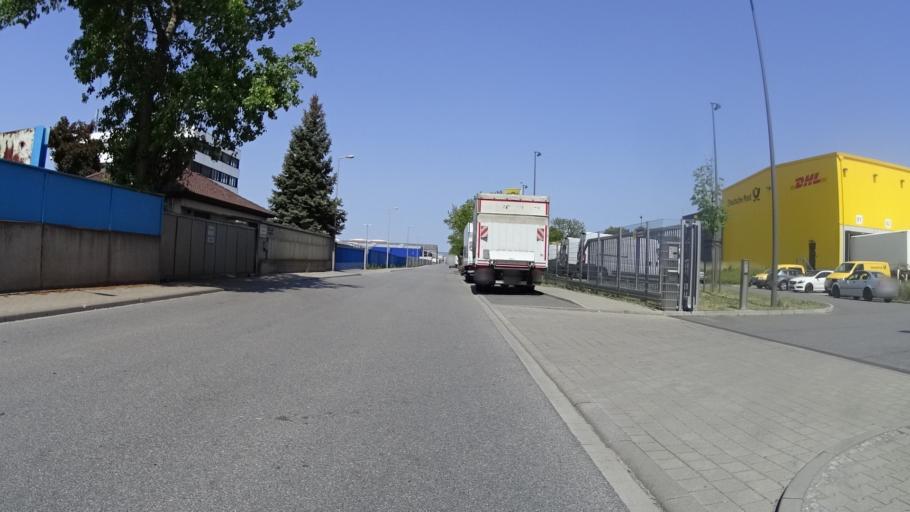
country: DE
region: Rheinland-Pfalz
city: Altrip
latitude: 49.4224
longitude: 8.5194
